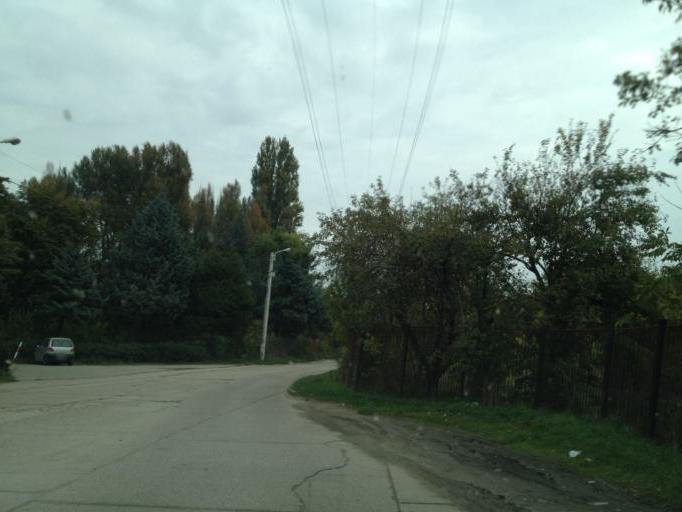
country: RO
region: Dolj
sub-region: Municipiul Craiova
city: Popoveni
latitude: 44.2955
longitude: 23.8004
